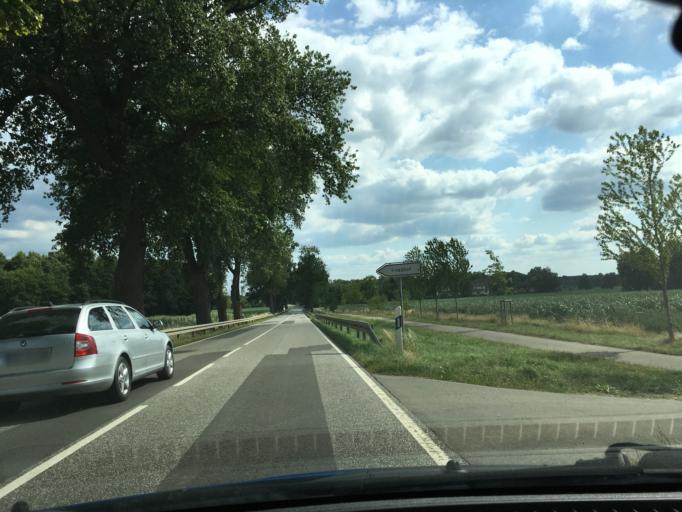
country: DE
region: Mecklenburg-Vorpommern
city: Lubtheen
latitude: 53.3718
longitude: 11.0851
